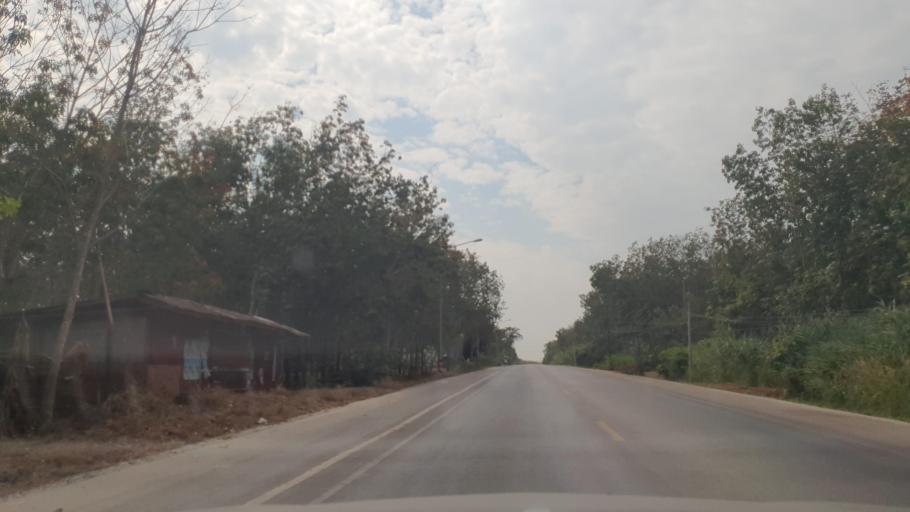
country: TH
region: Changwat Bueng Kan
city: Si Wilai
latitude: 18.2844
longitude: 103.7934
